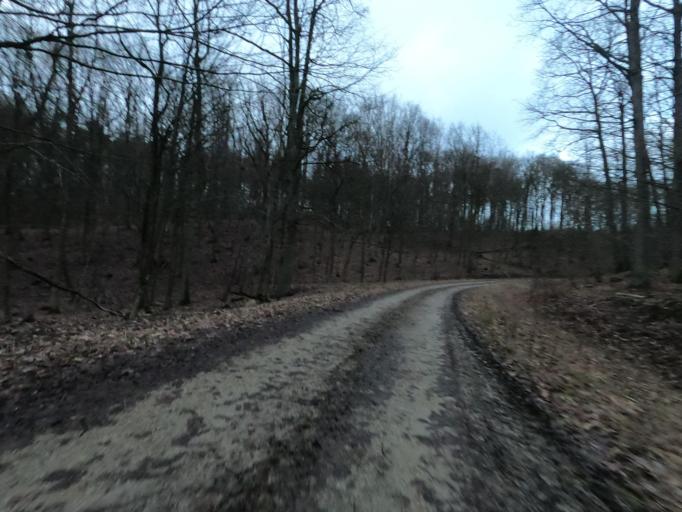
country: PL
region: Greater Poland Voivodeship
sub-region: Powiat pilski
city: Wyrzysk
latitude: 53.1216
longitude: 17.2192
